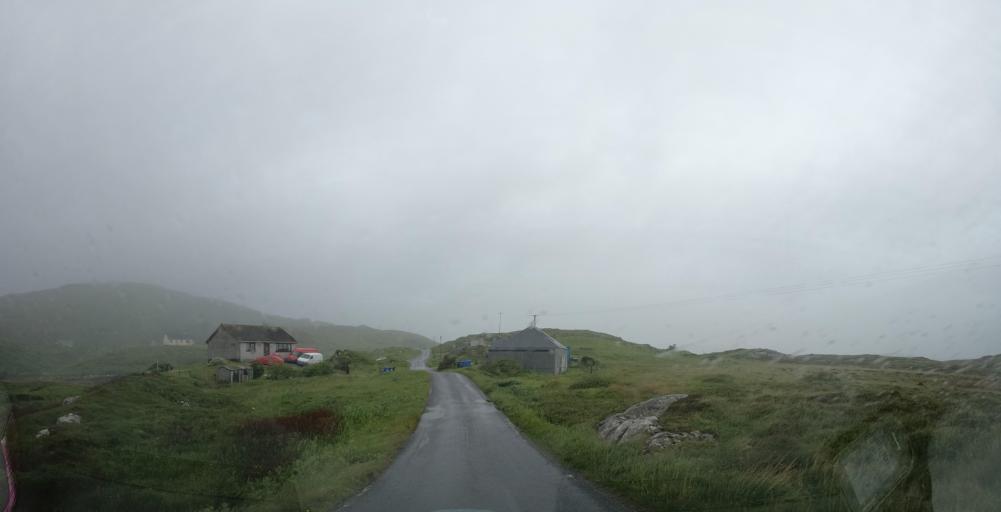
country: GB
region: Scotland
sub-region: Eilean Siar
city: Barra
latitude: 57.0113
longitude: -7.4255
